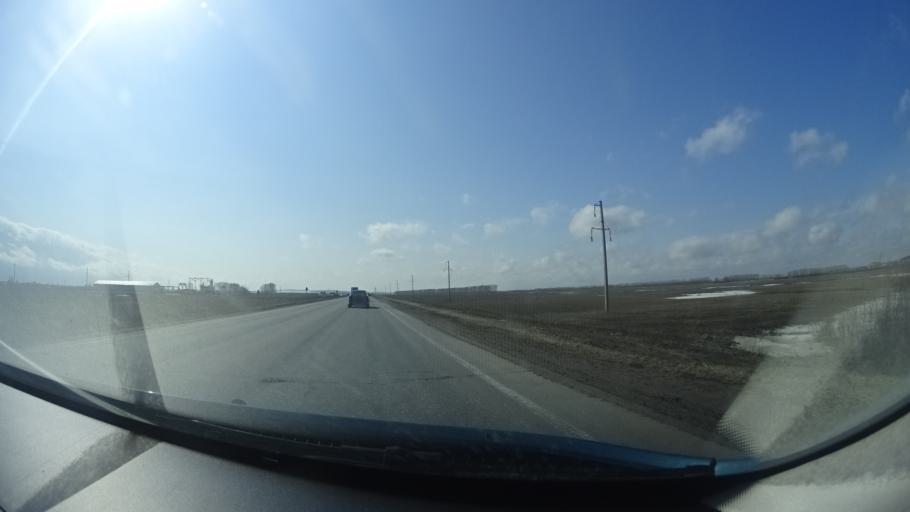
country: RU
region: Bashkortostan
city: Mikhaylovka
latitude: 54.9587
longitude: 55.7583
